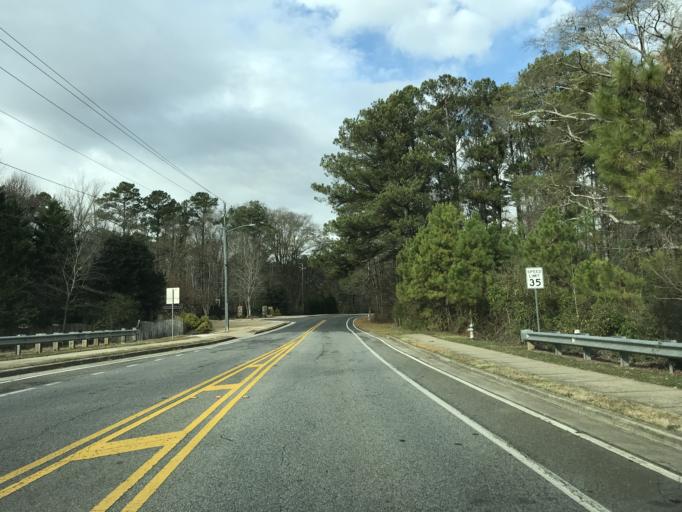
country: US
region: Georgia
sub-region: Fulton County
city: Alpharetta
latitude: 34.0881
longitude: -84.3091
